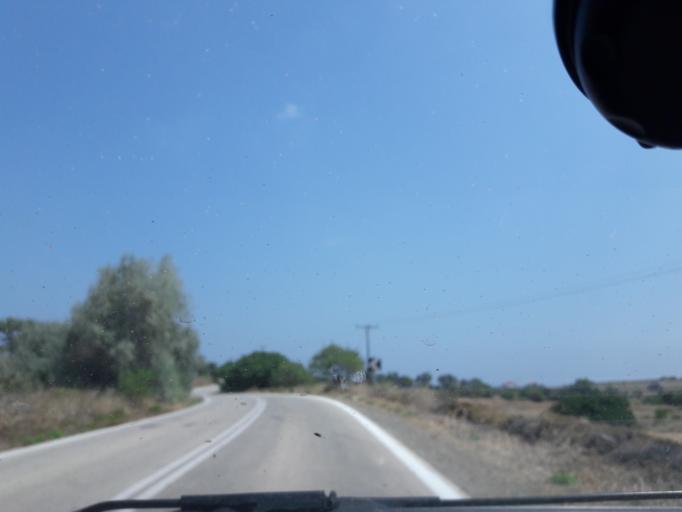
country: GR
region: North Aegean
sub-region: Nomos Lesvou
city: Myrina
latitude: 39.9250
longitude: 25.3246
